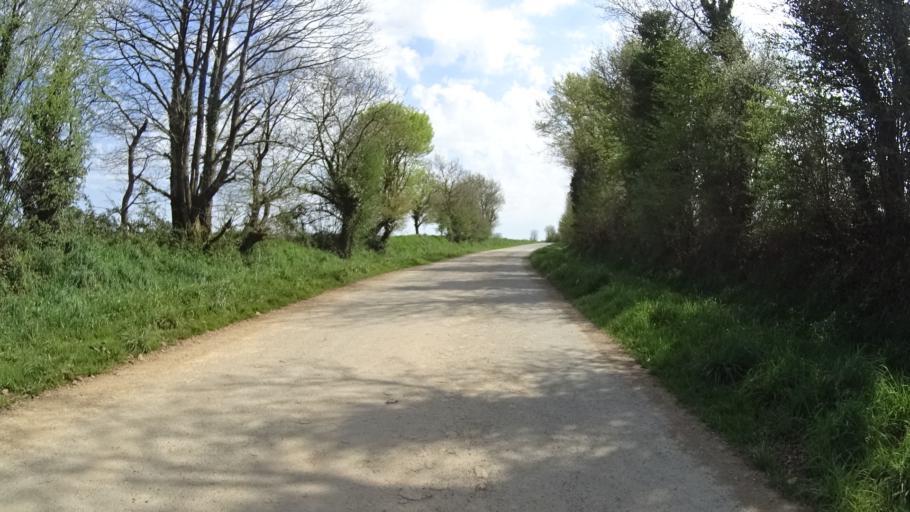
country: FR
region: Brittany
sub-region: Departement du Finistere
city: Sizun
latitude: 48.4331
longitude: -4.0997
